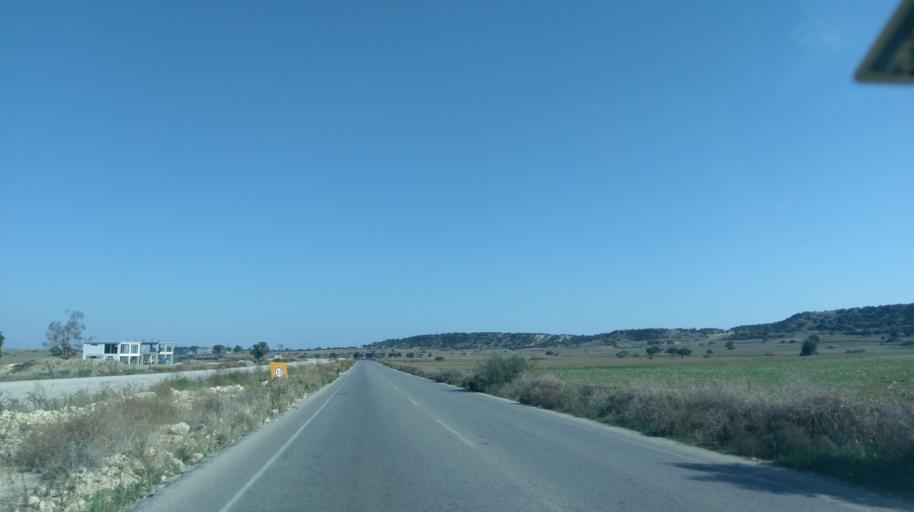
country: CY
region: Ammochostos
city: Trikomo
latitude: 35.3538
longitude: 34.0033
